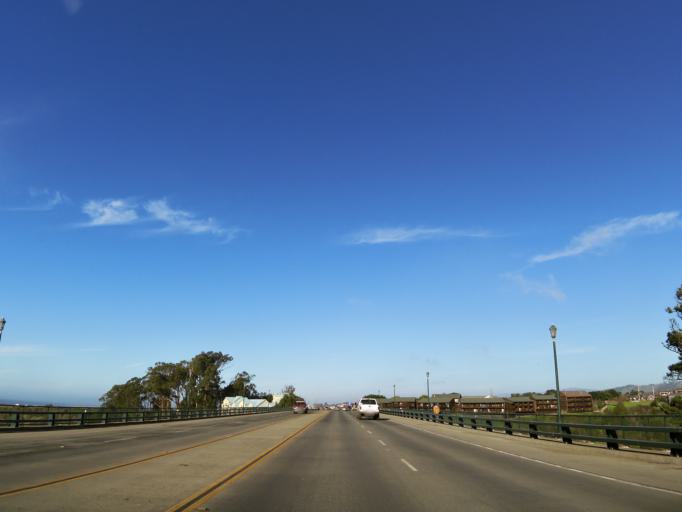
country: US
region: California
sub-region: Mendocino County
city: Fort Bragg
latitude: 39.4263
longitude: -123.8070
